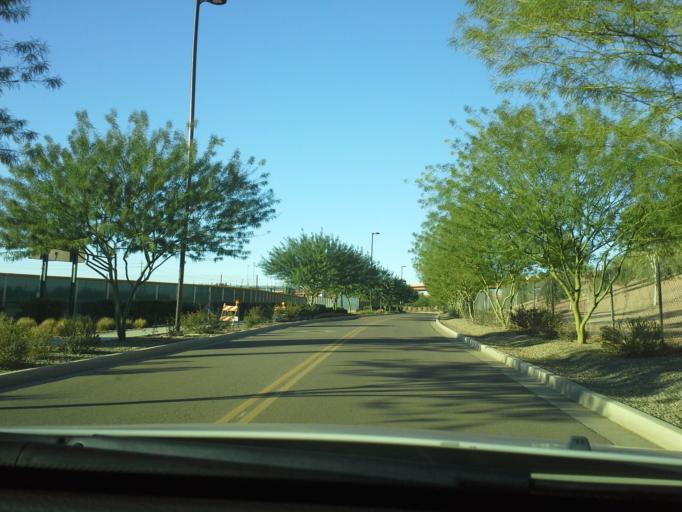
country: US
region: Arizona
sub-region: Maricopa County
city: Tempe
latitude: 33.4325
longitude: -111.8867
